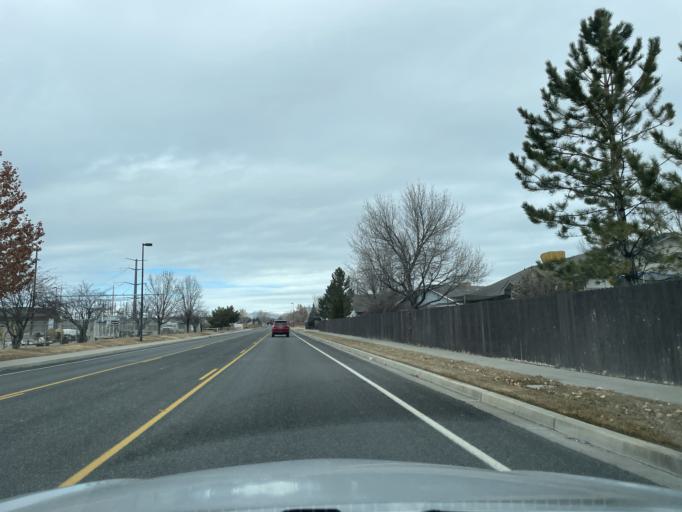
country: US
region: Colorado
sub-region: Mesa County
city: Grand Junction
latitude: 39.0971
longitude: -108.5801
